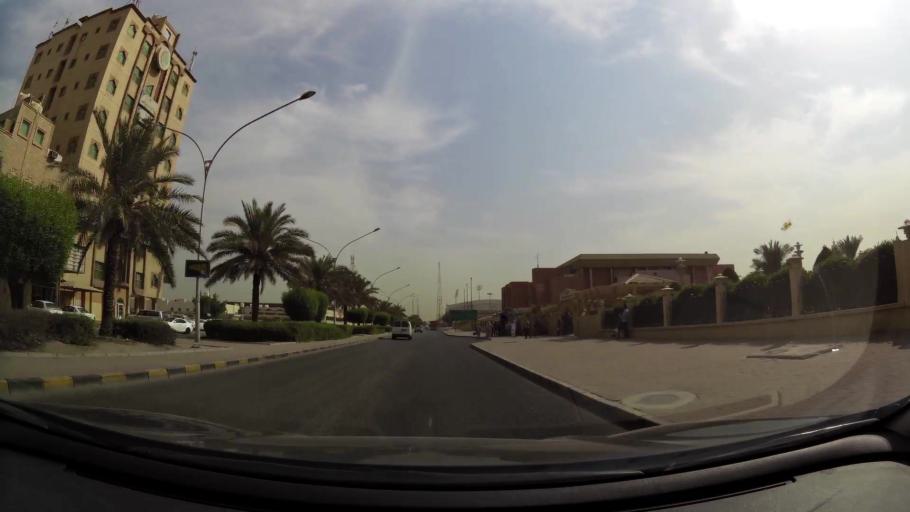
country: KW
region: Al Farwaniyah
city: Janub as Surrah
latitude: 29.2830
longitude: 47.9781
